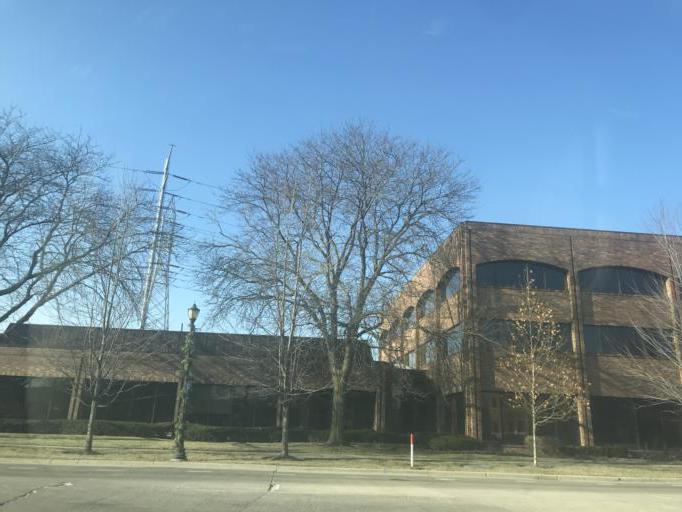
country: US
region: Illinois
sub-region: Cook County
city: Northfield
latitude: 42.1033
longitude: -87.7706
